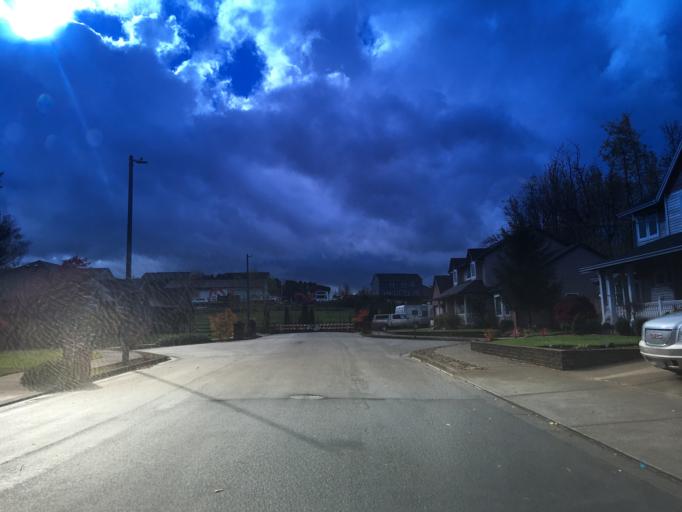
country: US
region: Oregon
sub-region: Multnomah County
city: Troutdale
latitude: 45.5091
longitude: -122.3809
